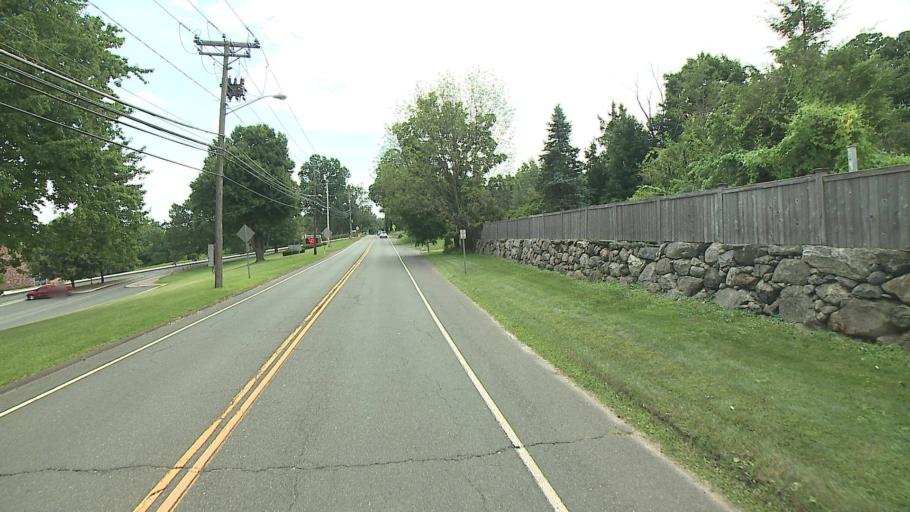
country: US
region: Connecticut
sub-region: Fairfield County
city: Danbury
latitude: 41.4162
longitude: -73.4724
